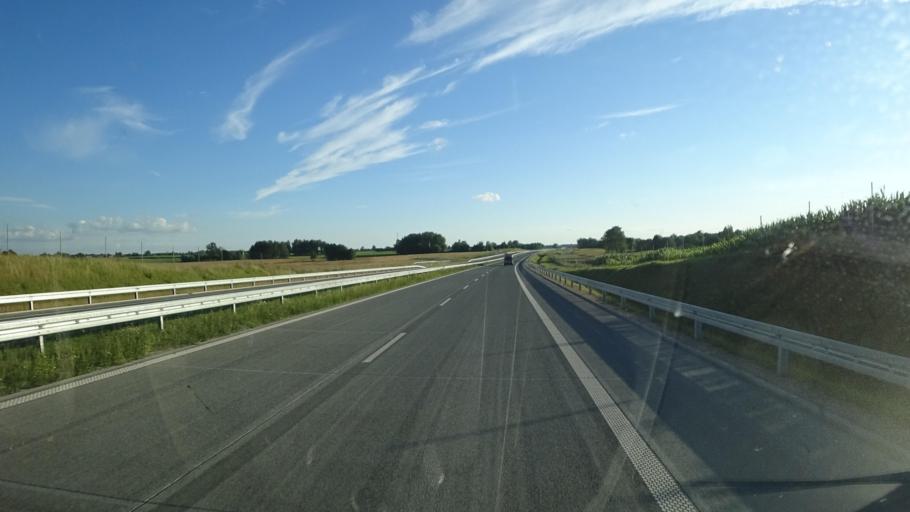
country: PL
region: Podlasie
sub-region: Powiat suwalski
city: Raczki
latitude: 53.9205
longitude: 22.7433
